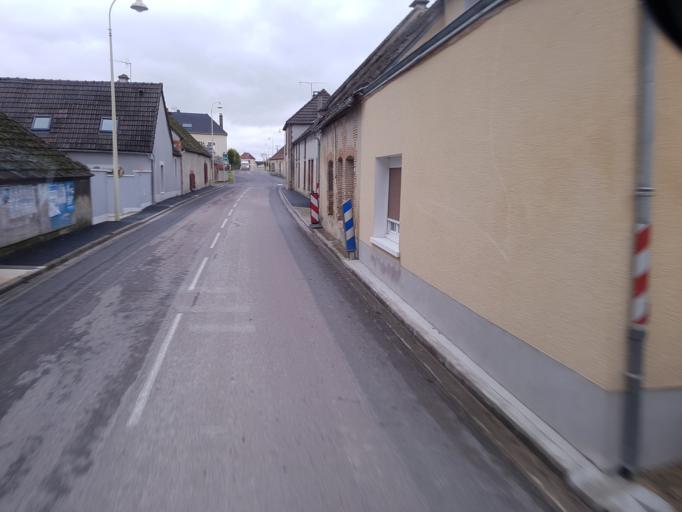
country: FR
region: Champagne-Ardenne
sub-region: Departement de la Marne
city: Saint-Just-Sauvage
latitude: 48.5825
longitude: 3.8523
